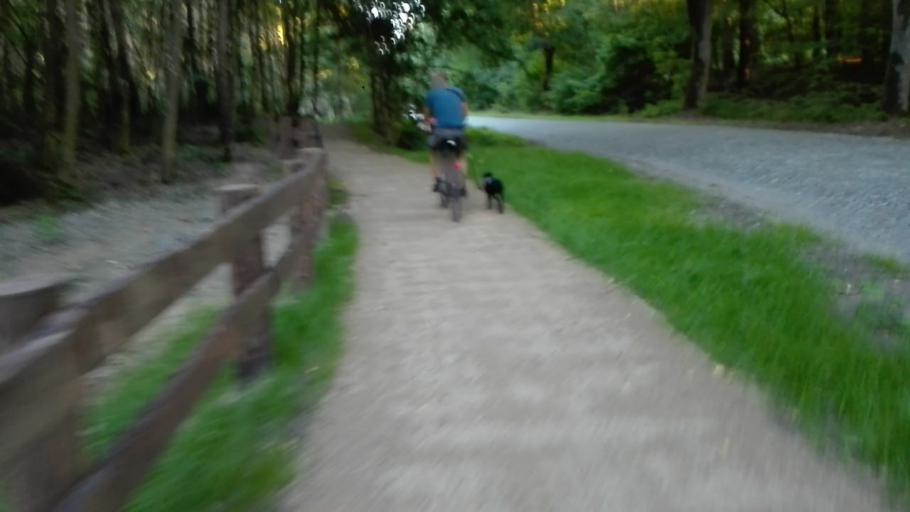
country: PL
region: West Pomeranian Voivodeship
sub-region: Powiat policki
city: Dobra
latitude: 53.4681
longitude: 14.3624
